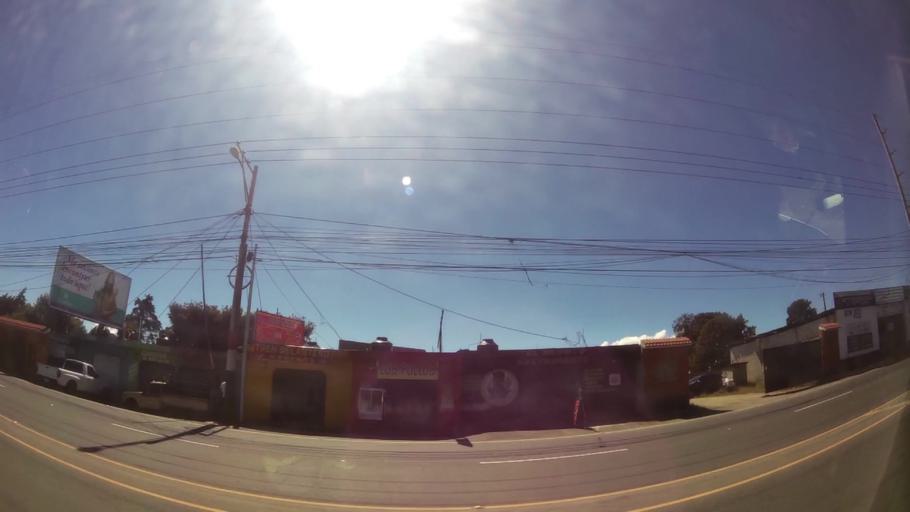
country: GT
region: Guatemala
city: San Jose Pinula
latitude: 14.5431
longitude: -90.4392
